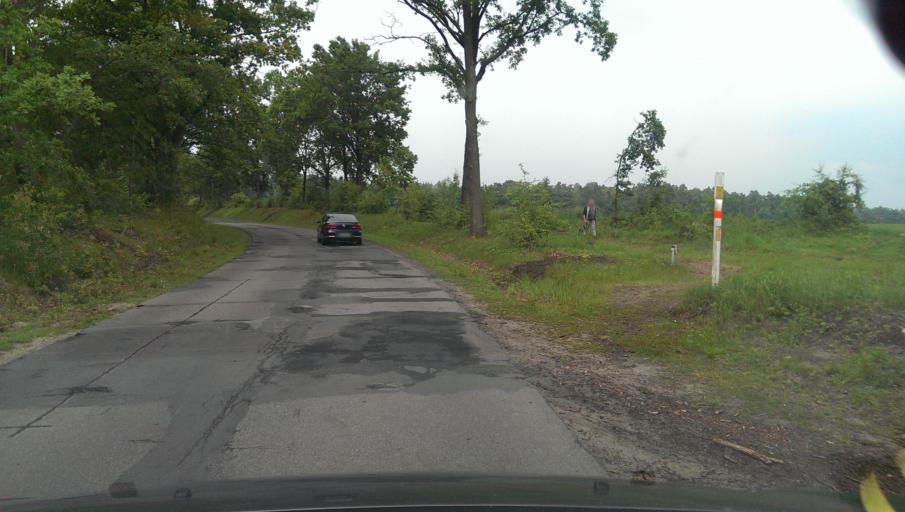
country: DE
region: Lower Saxony
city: Fassberg
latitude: 52.8914
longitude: 10.1648
